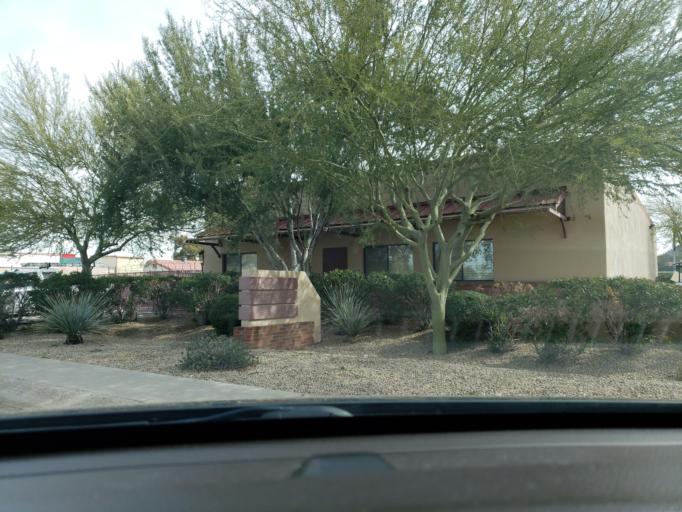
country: US
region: Arizona
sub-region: Maricopa County
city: Phoenix
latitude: 33.5668
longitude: -112.0706
